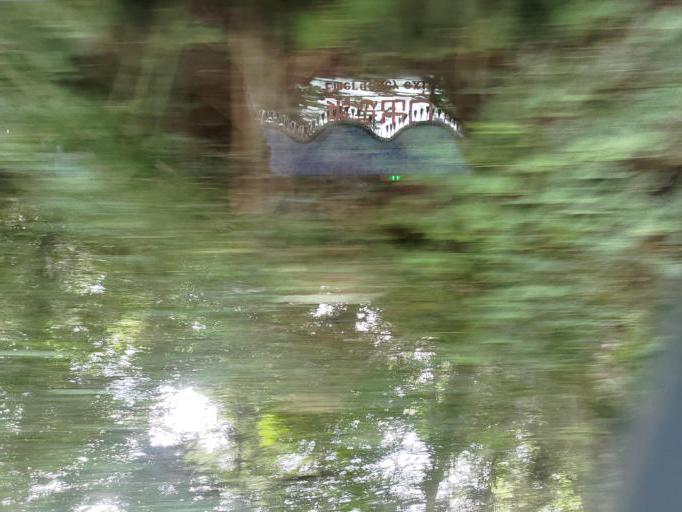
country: TW
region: Taiwan
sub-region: Hsinchu
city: Hsinchu
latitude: 24.6200
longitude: 121.0452
